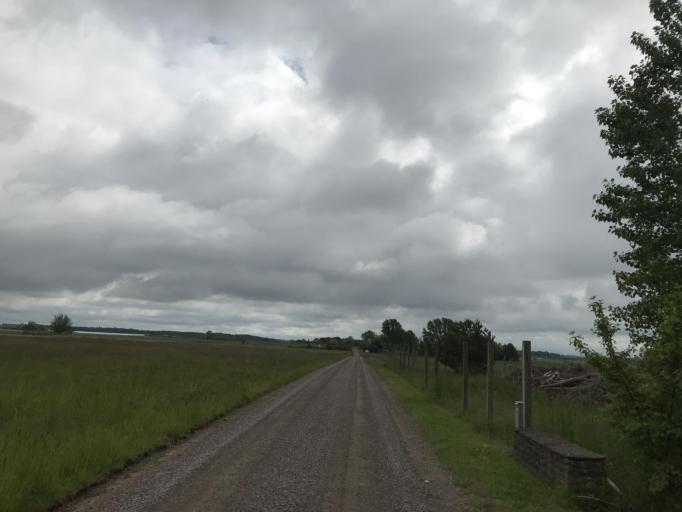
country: SE
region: Skane
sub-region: Landskrona
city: Asmundtorp
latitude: 55.8701
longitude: 12.9094
